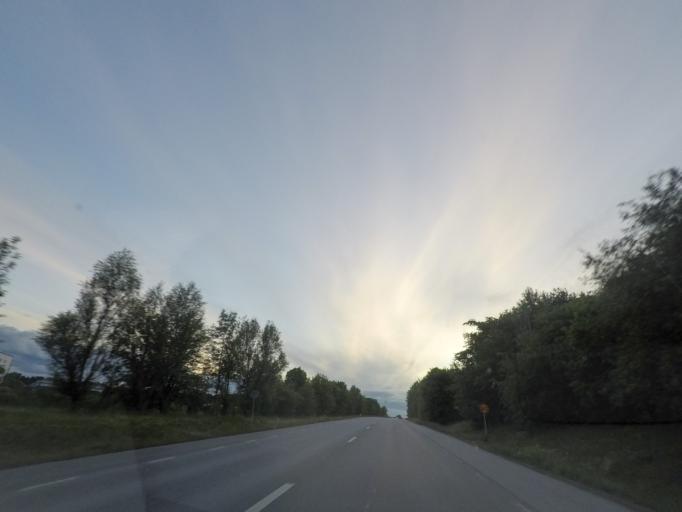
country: SE
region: Stockholm
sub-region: Sigtuna Kommun
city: Marsta
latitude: 59.6183
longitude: 17.8468
